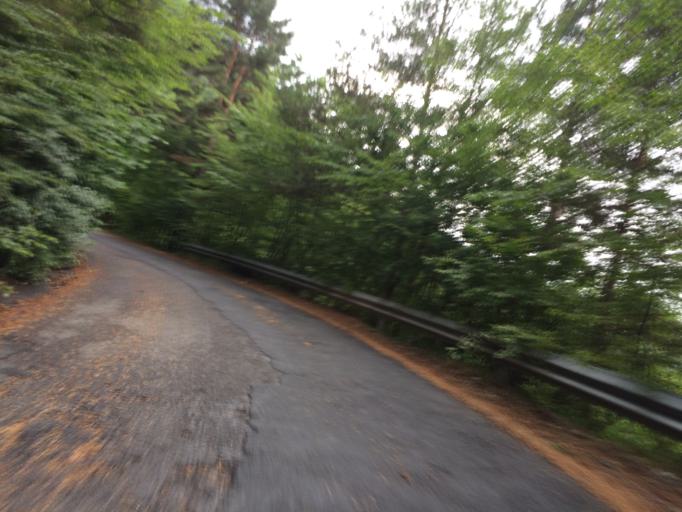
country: IT
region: Liguria
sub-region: Provincia di Imperia
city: Triora
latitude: 43.9822
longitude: 7.7482
